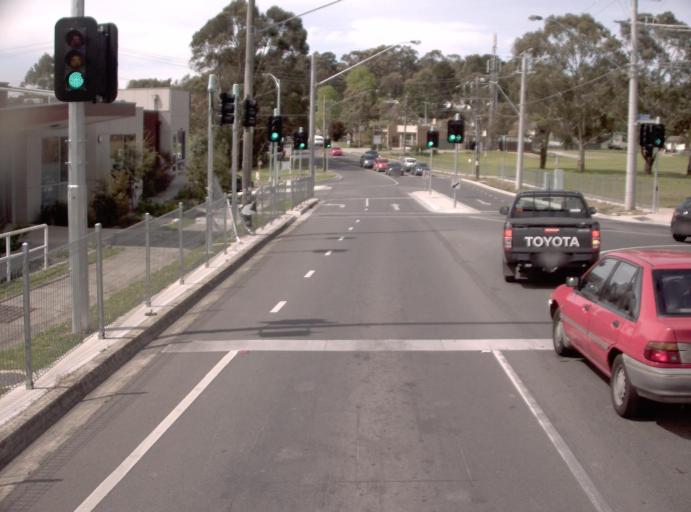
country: AU
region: Victoria
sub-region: Yarra Ranges
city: Kilsyth
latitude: -37.7866
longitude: 145.3184
